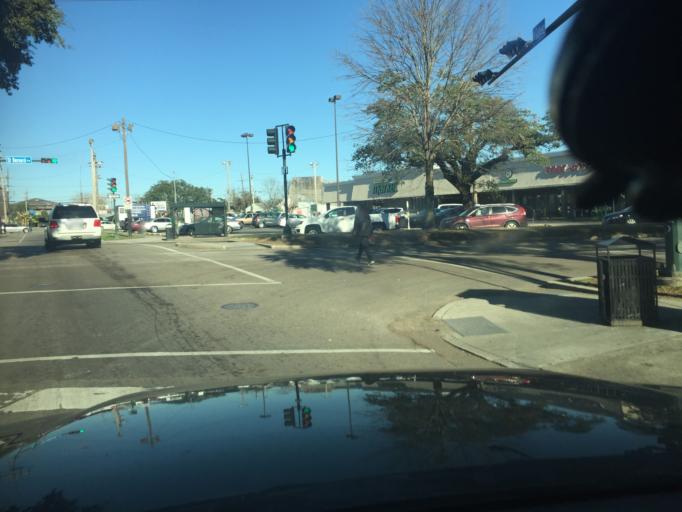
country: US
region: Louisiana
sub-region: Orleans Parish
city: New Orleans
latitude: 29.9774
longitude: -90.0686
